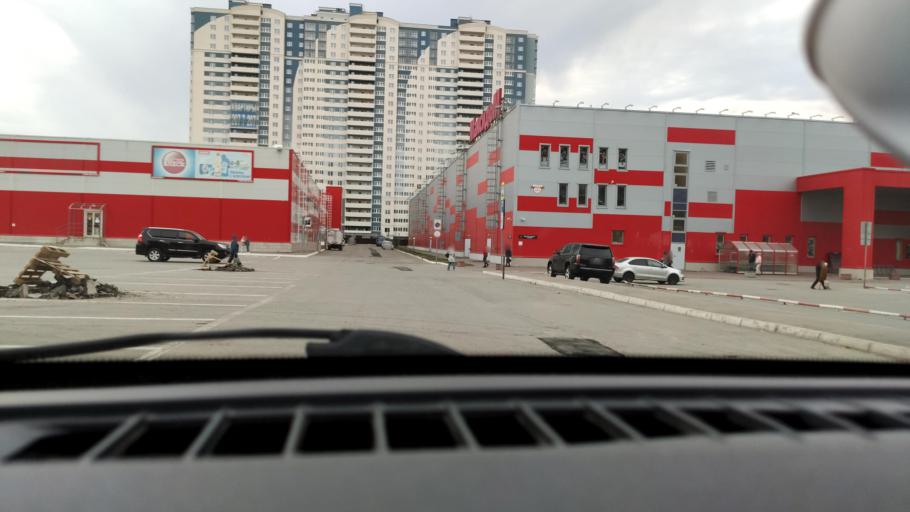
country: RU
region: Samara
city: Samara
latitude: 53.2529
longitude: 50.2195
